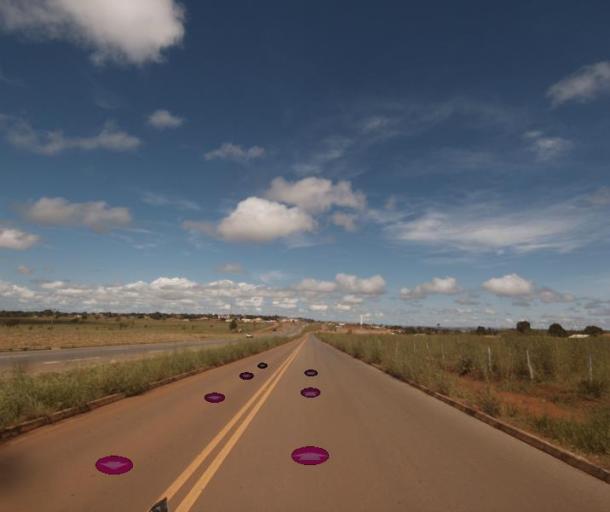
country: BR
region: Federal District
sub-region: Brasilia
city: Brasilia
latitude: -15.7470
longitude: -48.3208
